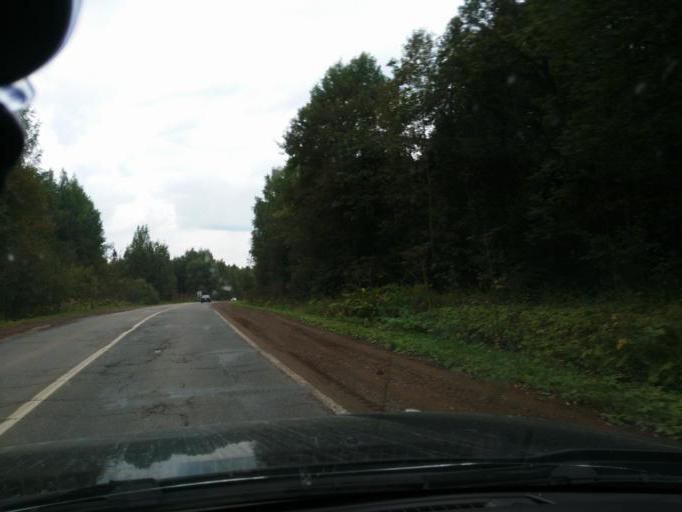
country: RU
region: Perm
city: Chernushka
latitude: 56.6759
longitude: 56.1712
